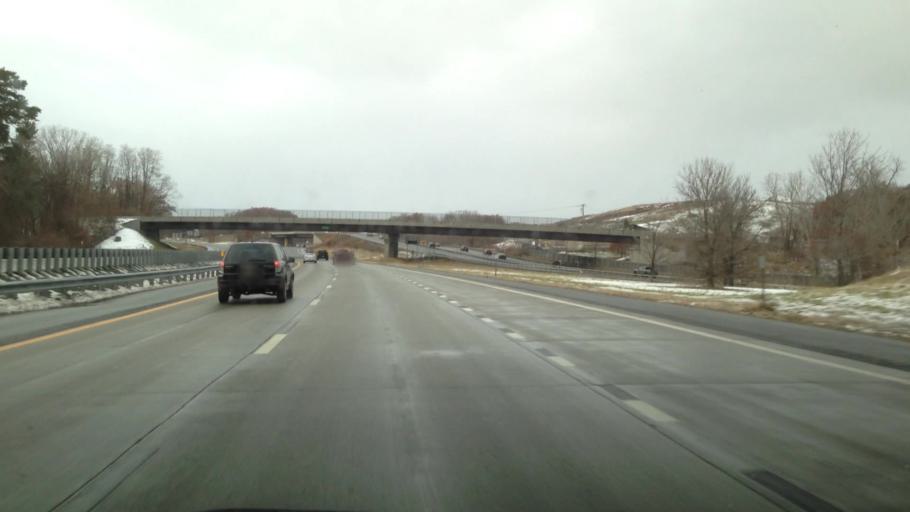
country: US
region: New York
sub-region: Albany County
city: McKownville
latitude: 42.7015
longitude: -73.8486
